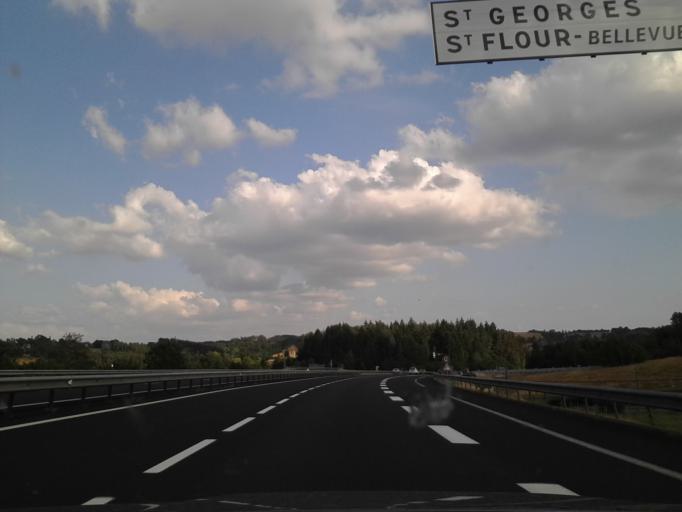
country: FR
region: Auvergne
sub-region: Departement du Cantal
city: Saint-Flour
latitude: 45.0318
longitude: 3.1427
